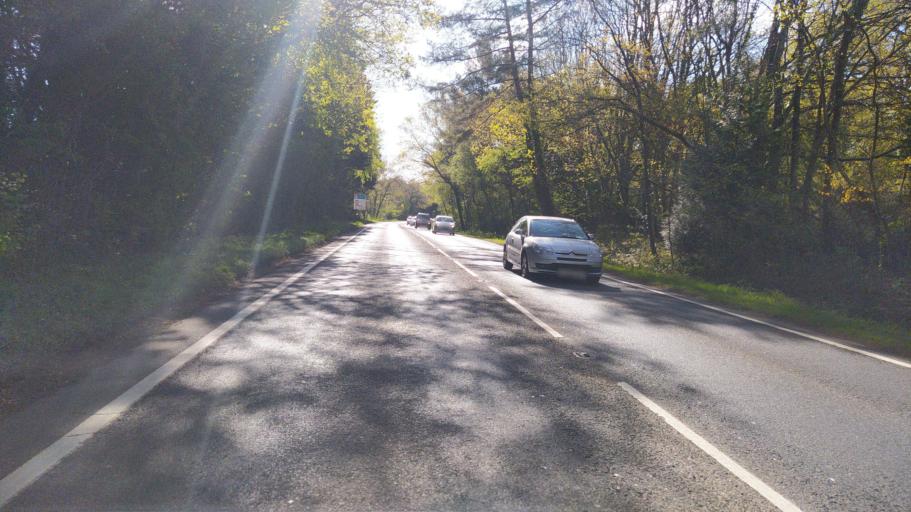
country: GB
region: England
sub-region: Hampshire
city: Marchwood
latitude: 50.8843
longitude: -1.4507
